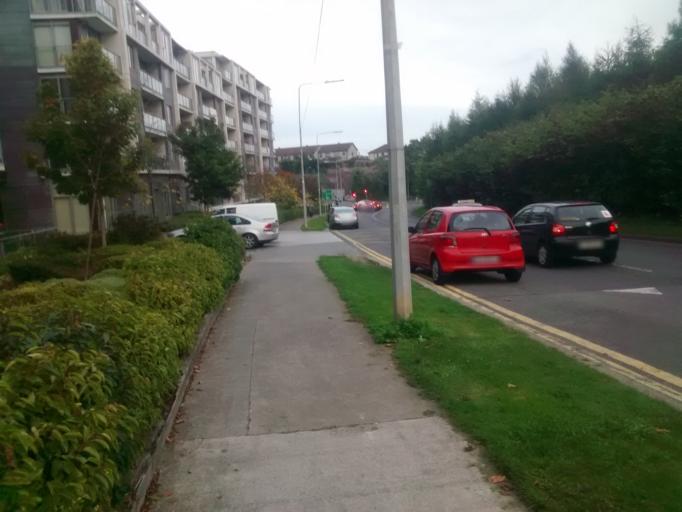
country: IE
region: Leinster
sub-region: Dublin City
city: Finglas
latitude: 53.3798
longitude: -6.2907
